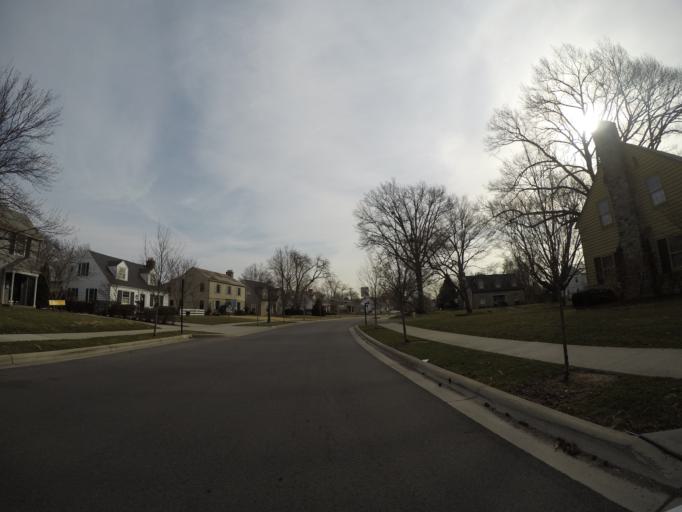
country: US
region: Ohio
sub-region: Franklin County
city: Upper Arlington
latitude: 39.9989
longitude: -83.0557
